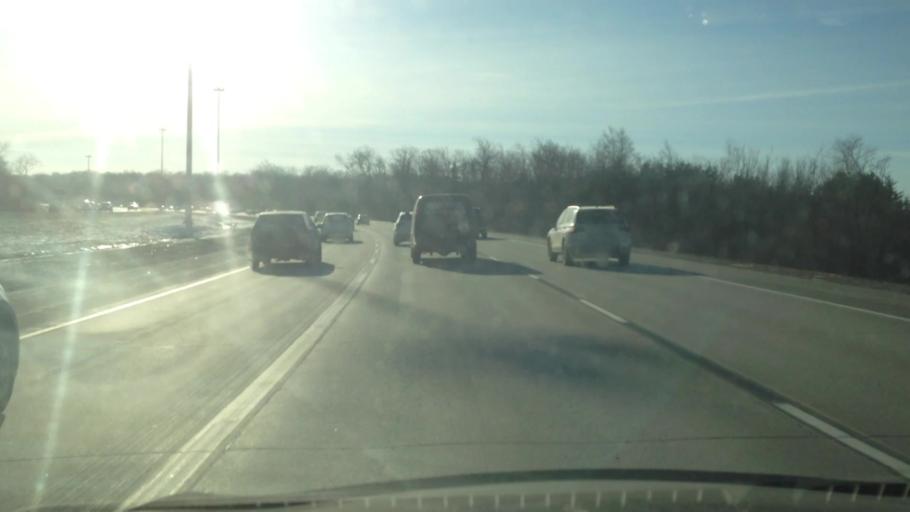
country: CA
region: Quebec
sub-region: Laurentides
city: Saint-Jerome
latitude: 45.7173
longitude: -73.9712
